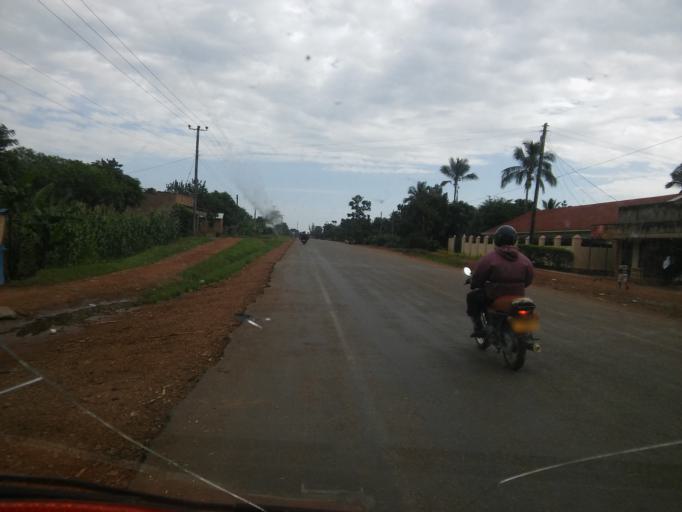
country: UG
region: Eastern Region
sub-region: Mbale District
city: Mbale
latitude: 1.1258
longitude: 34.1681
